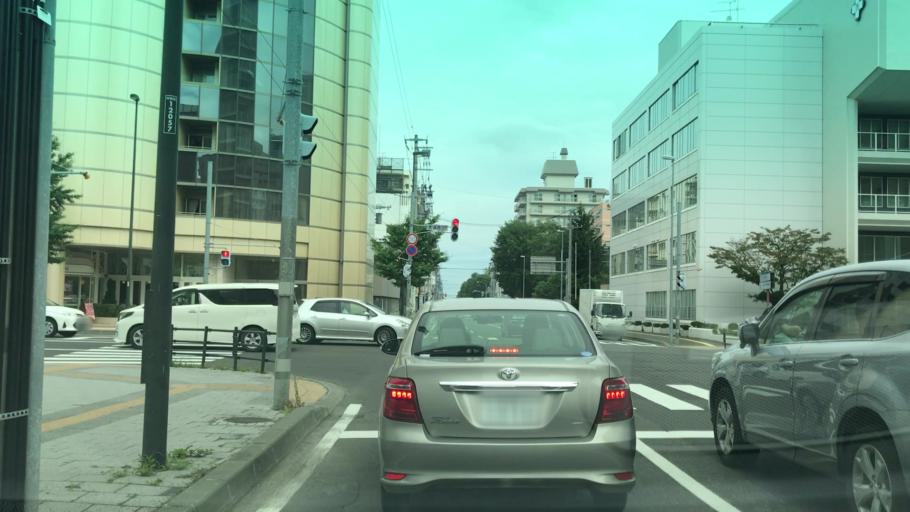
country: JP
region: Hokkaido
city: Sapporo
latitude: 43.0566
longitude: 141.3273
